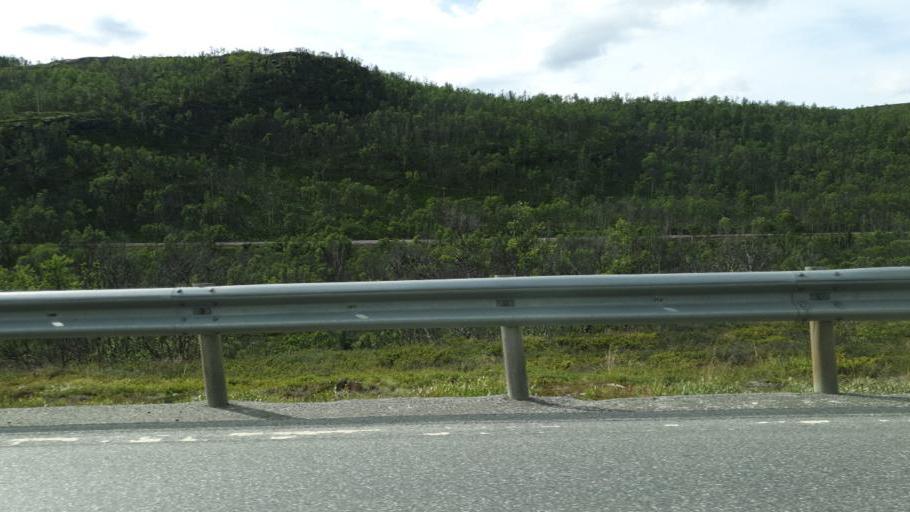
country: NO
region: Sor-Trondelag
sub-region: Oppdal
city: Oppdal
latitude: 62.2962
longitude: 9.5955
